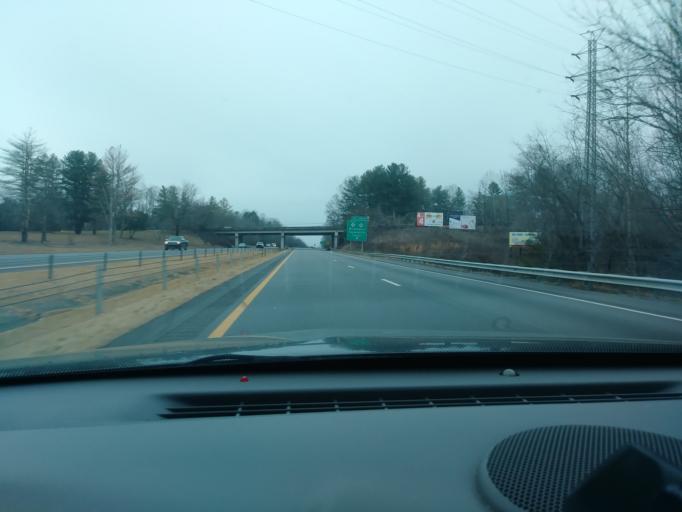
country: US
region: North Carolina
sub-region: Wilkes County
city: Wilkesboro
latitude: 36.1365
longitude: -81.1590
